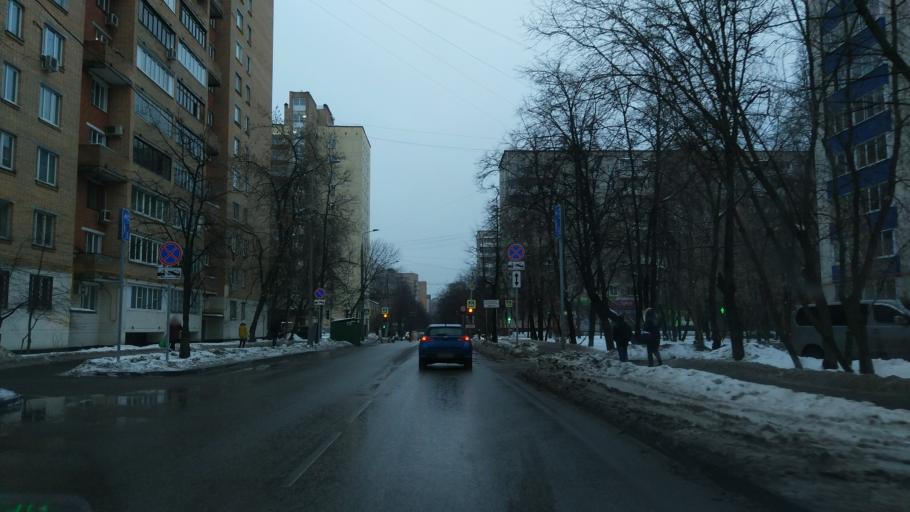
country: RU
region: Moskovskaya
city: Izmaylovo
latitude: 55.7912
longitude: 37.8071
